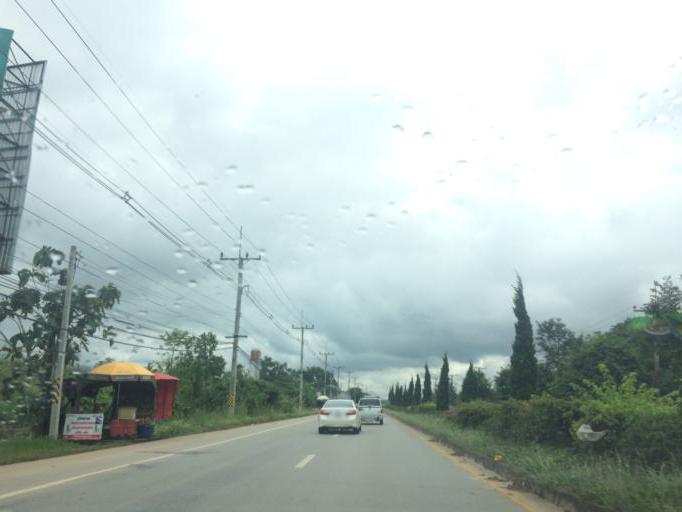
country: TH
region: Chiang Rai
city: Chiang Rai
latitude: 20.0136
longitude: 99.8691
